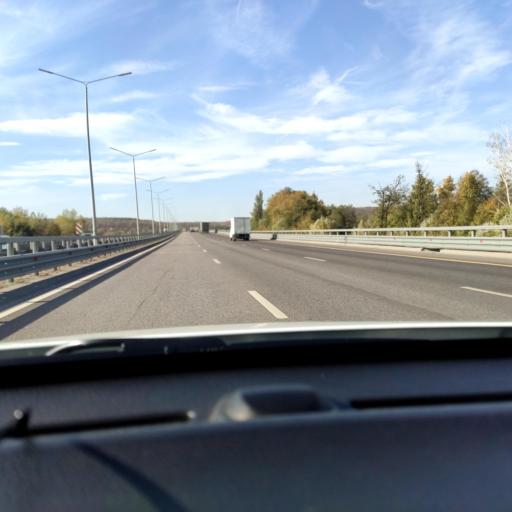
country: RU
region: Voronezj
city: Somovo
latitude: 51.7905
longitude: 39.2751
